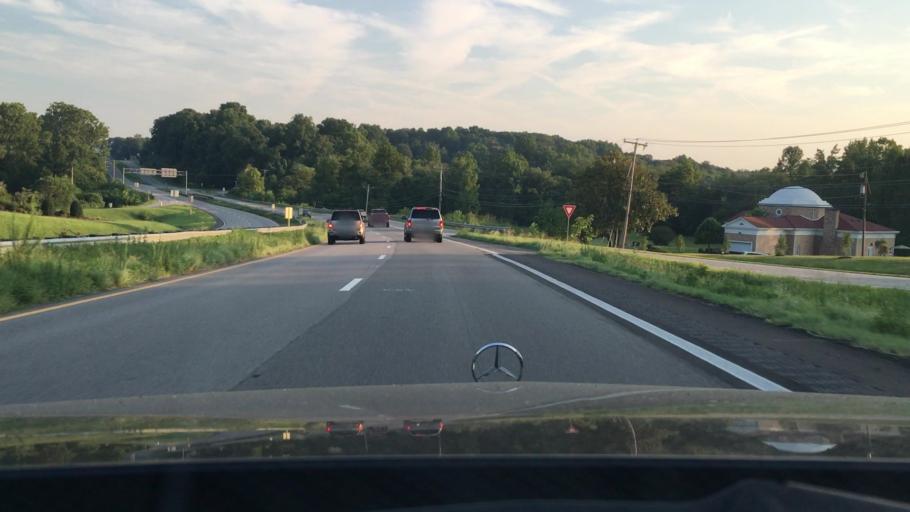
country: US
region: Virginia
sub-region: Pittsylvania County
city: Chatham
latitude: 36.8062
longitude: -79.3929
